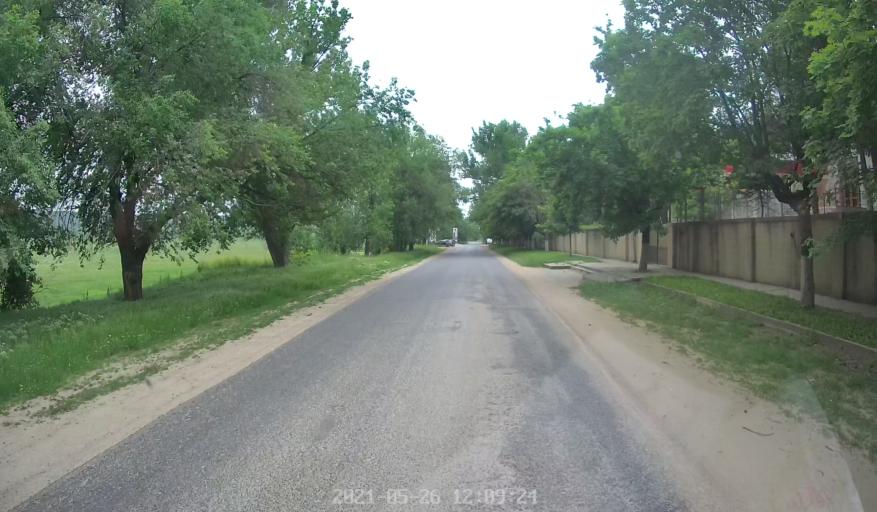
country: MD
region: Hincesti
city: Dancu
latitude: 46.7704
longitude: 28.3463
